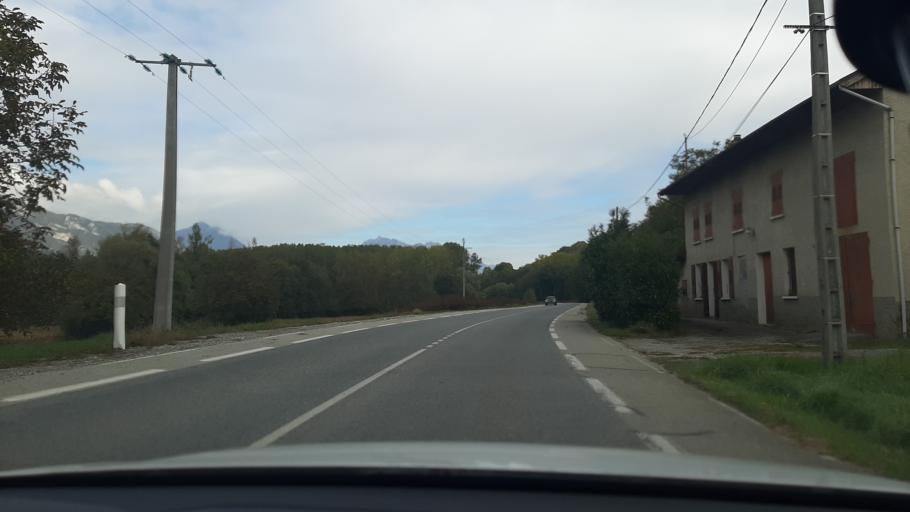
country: FR
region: Rhone-Alpes
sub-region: Departement de l'Isere
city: Pontcharra
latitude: 45.4518
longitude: 6.0427
